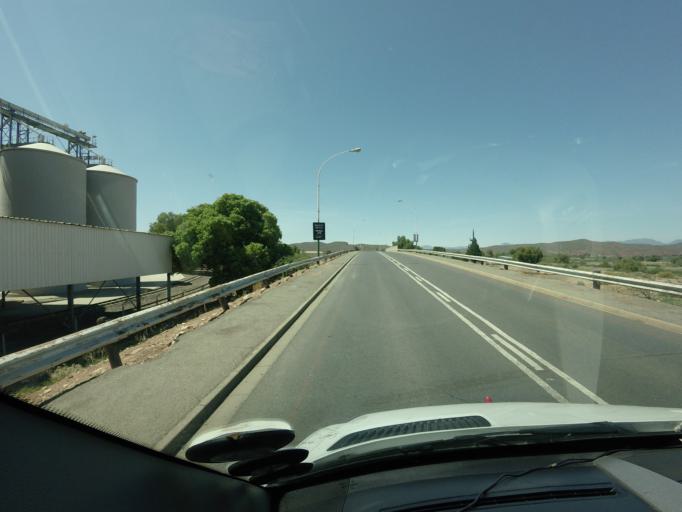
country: ZA
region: Western Cape
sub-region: Eden District Municipality
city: Oudtshoorn
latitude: -33.6105
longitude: 22.2136
